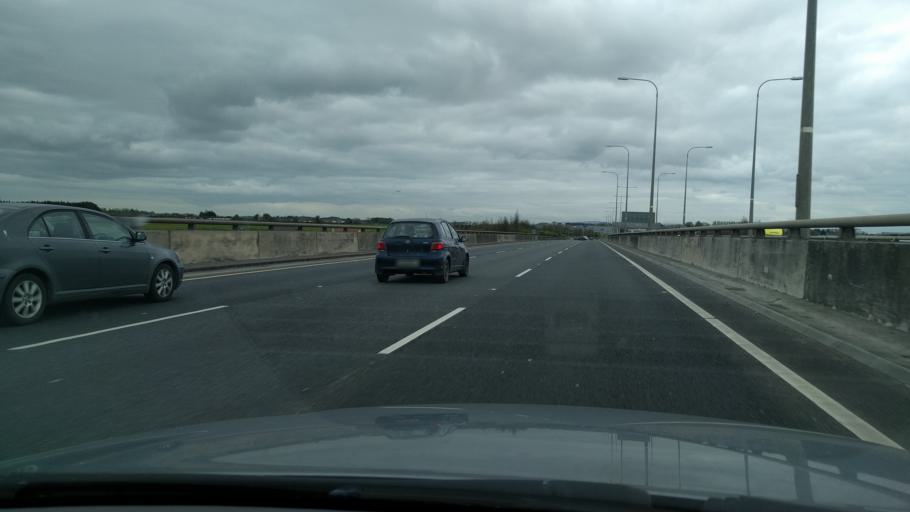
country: IE
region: Leinster
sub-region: Fingal County
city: Swords
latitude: 53.4655
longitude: -6.2026
